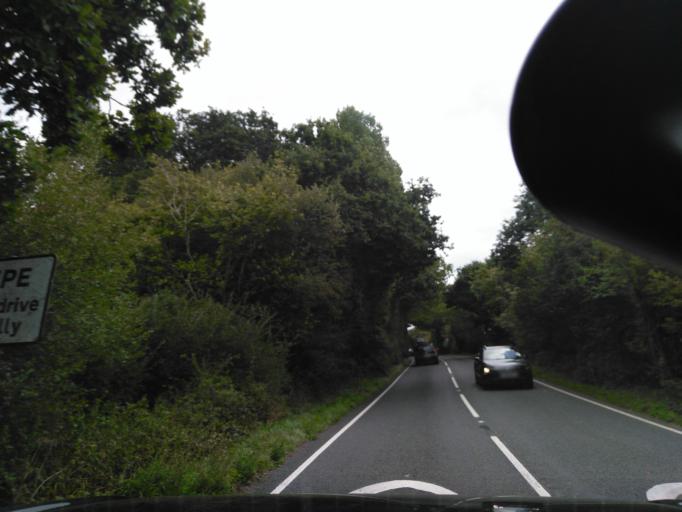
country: GB
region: England
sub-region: Dorset
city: Lytchett Matravers
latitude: 50.7401
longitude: -2.1107
